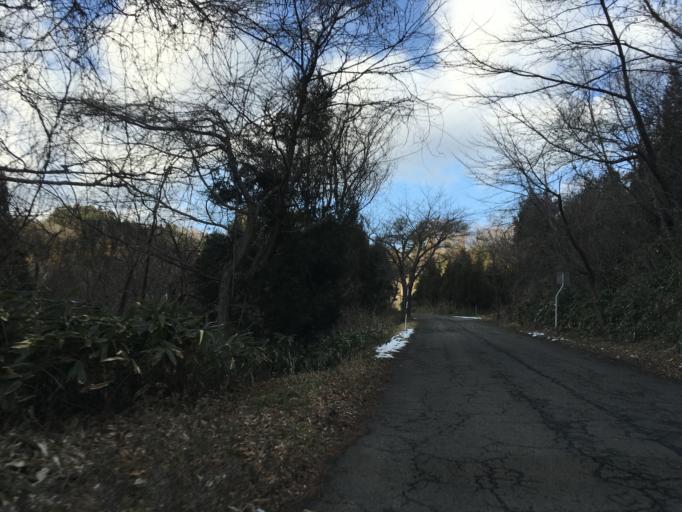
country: JP
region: Miyagi
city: Furukawa
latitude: 38.8168
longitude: 140.8330
